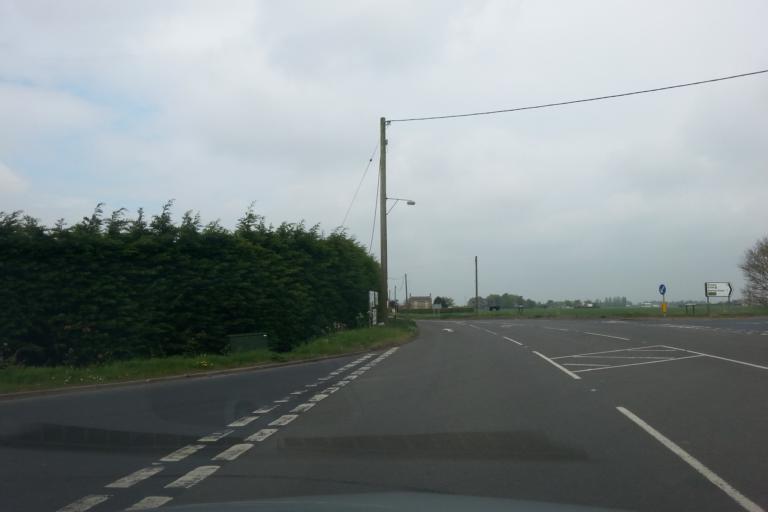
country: GB
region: England
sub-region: Norfolk
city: Outwell
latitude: 52.5641
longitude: 0.2287
